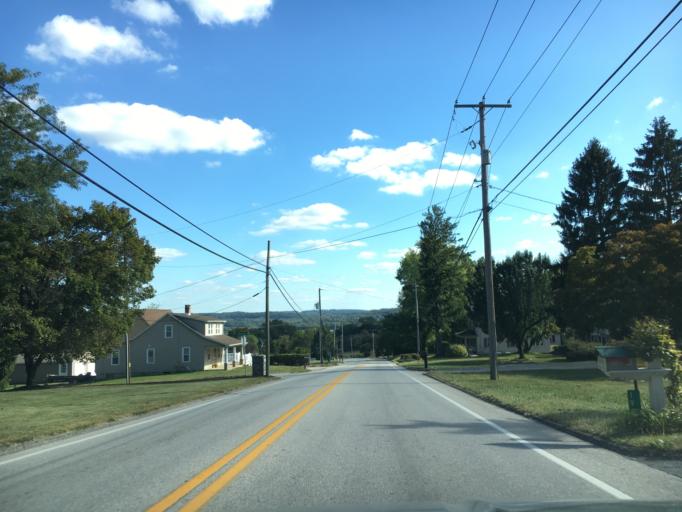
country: US
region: Pennsylvania
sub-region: York County
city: East York
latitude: 39.9977
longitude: -76.6771
